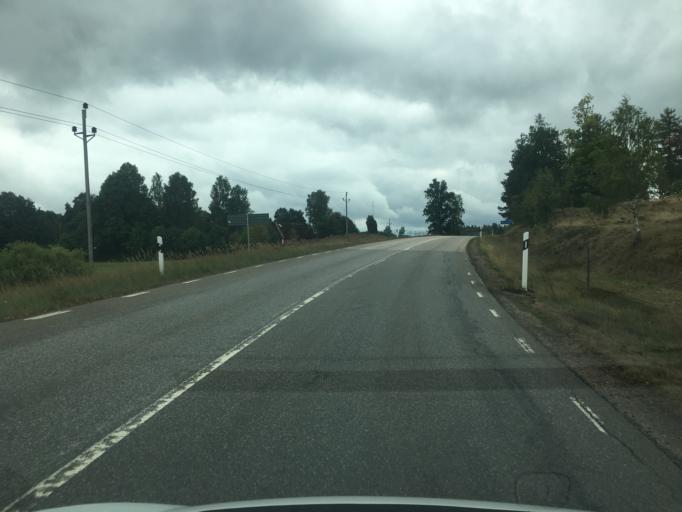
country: SE
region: Kronoberg
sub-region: Ljungby Kommun
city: Lagan
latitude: 56.9603
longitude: 14.0076
